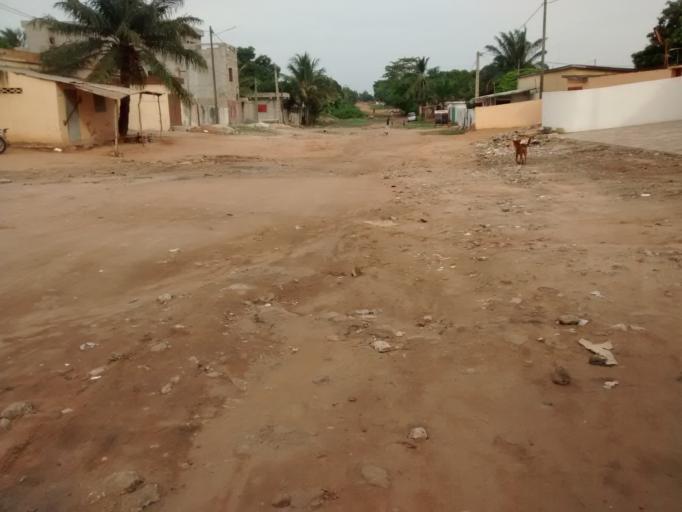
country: TG
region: Maritime
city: Lome
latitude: 6.1764
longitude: 1.1839
